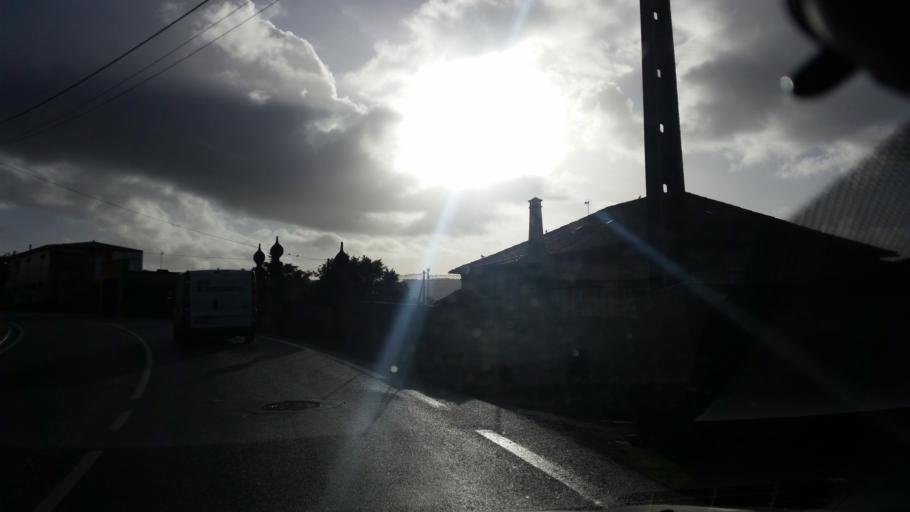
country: PT
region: Braga
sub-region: Guimaraes
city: Lordelo
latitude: 41.3705
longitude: -8.3750
